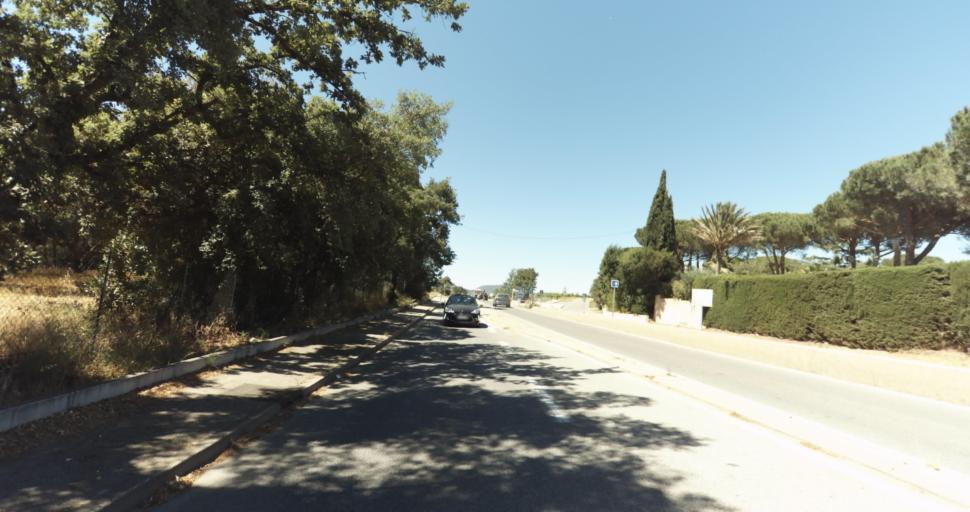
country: FR
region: Provence-Alpes-Cote d'Azur
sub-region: Departement du Var
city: Gassin
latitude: 43.2312
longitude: 6.5751
